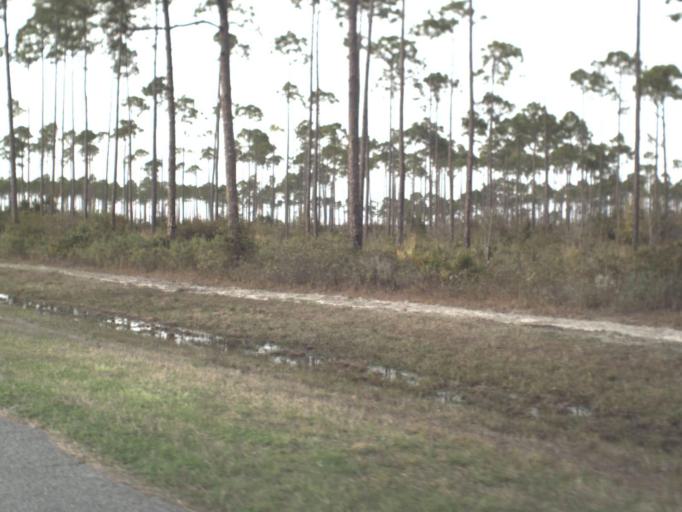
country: US
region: Florida
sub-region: Bay County
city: Tyndall Air Force Base
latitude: 30.0450
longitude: -85.5577
